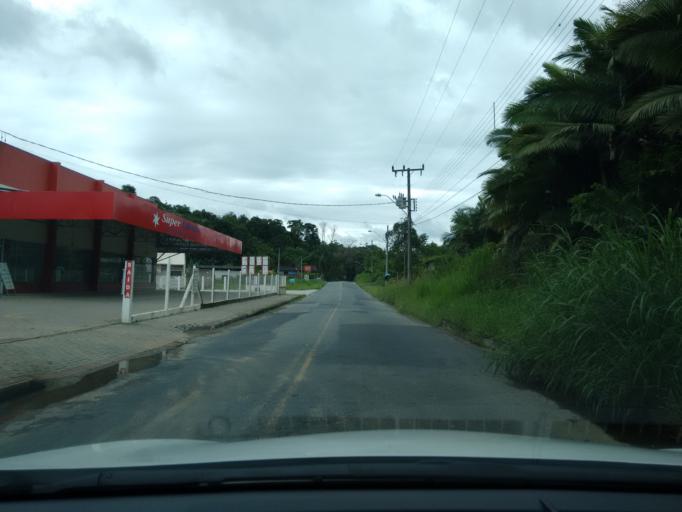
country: BR
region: Santa Catarina
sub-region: Blumenau
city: Blumenau
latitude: -26.8632
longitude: -49.1376
